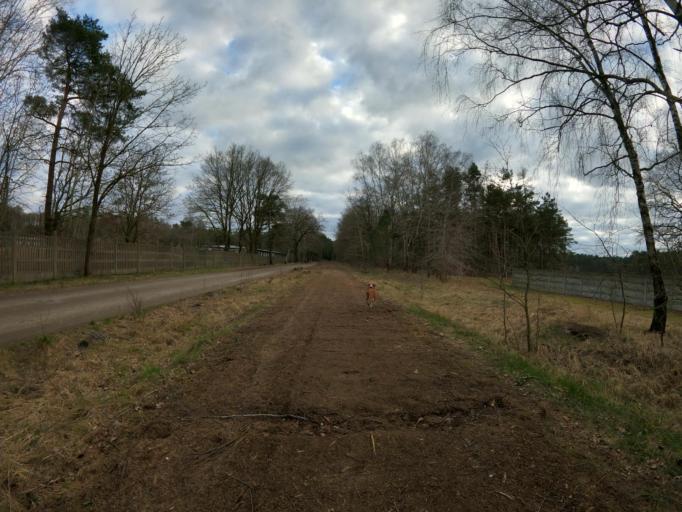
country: PL
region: West Pomeranian Voivodeship
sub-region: Powiat kamienski
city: Golczewo
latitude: 53.8364
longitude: 15.0031
